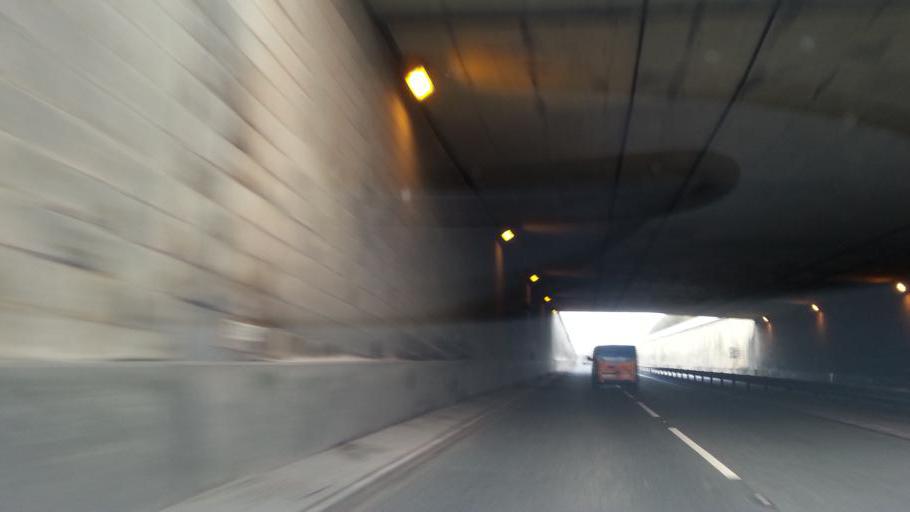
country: GB
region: England
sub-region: Bath and North East Somerset
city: Bath
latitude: 51.4024
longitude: -2.3388
